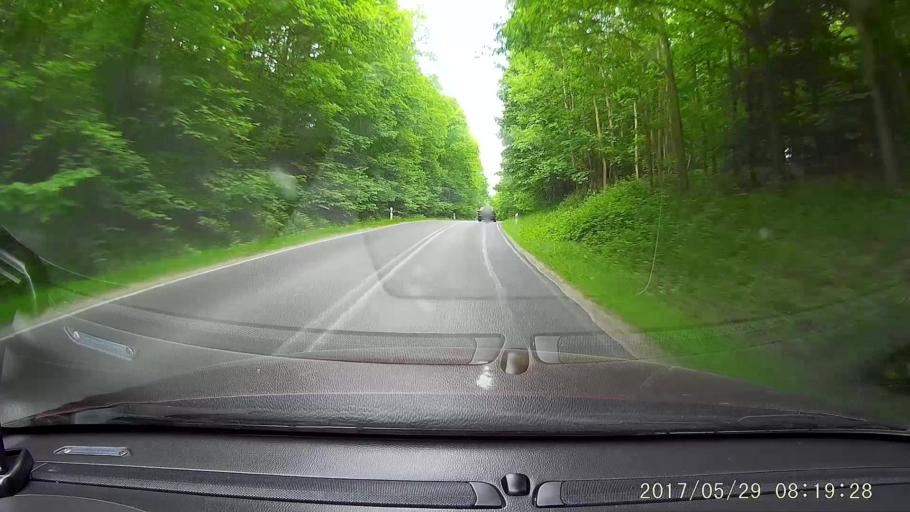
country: PL
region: Lower Silesian Voivodeship
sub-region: Powiat zlotoryjski
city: Zlotoryja
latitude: 51.1024
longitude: 15.8860
